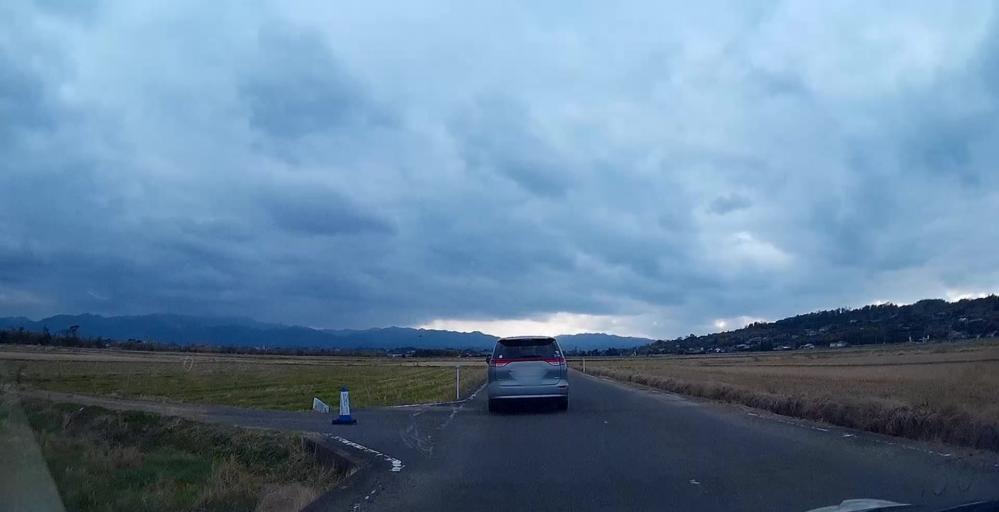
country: JP
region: Kagoshima
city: Izumi
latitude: 32.1014
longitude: 130.2751
